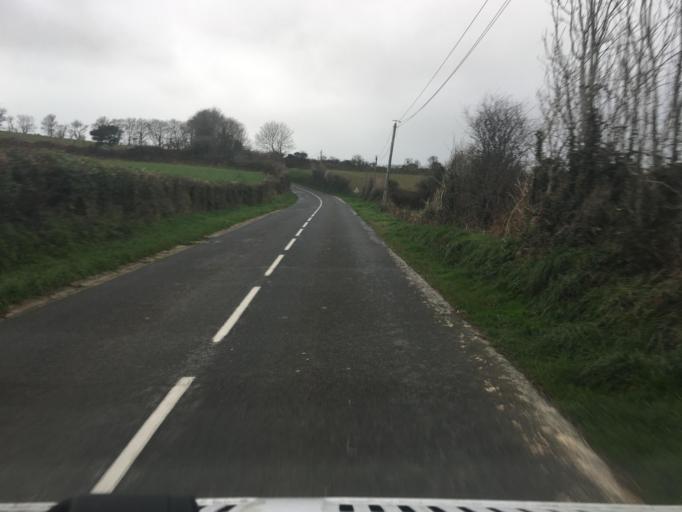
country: FR
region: Lower Normandy
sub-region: Departement de la Manche
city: Beaumont-Hague
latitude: 49.6820
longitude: -1.8536
